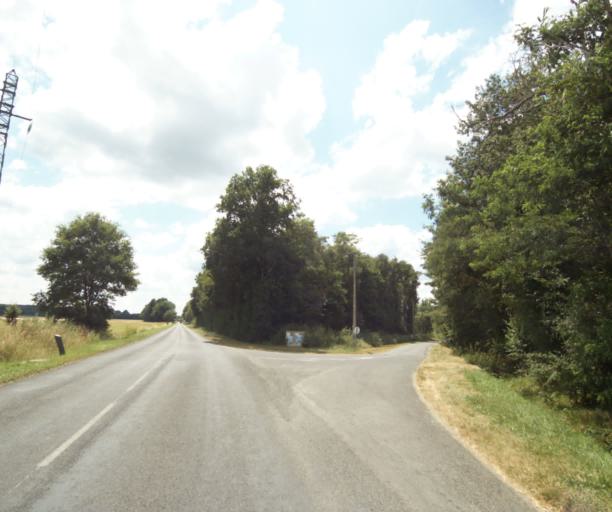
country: FR
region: Ile-de-France
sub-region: Departement de Seine-et-Marne
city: Vulaines-sur-Seine
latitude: 48.4401
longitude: 2.7760
